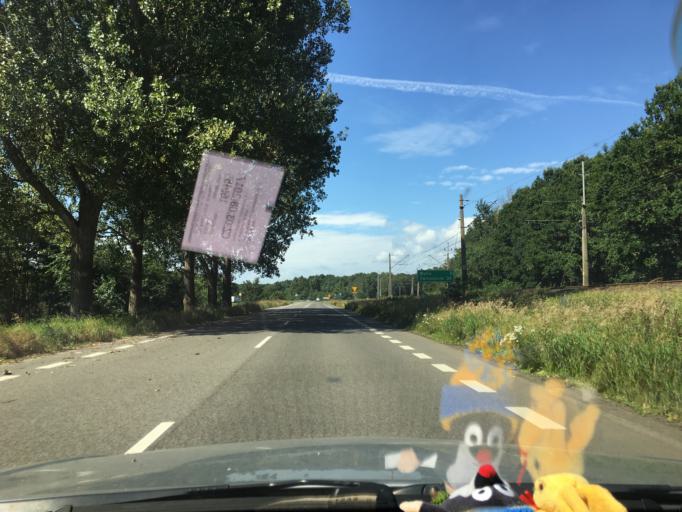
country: PL
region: West Pomeranian Voivodeship
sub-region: Powiat kamienski
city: Wolin
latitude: 53.8438
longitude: 14.7123
